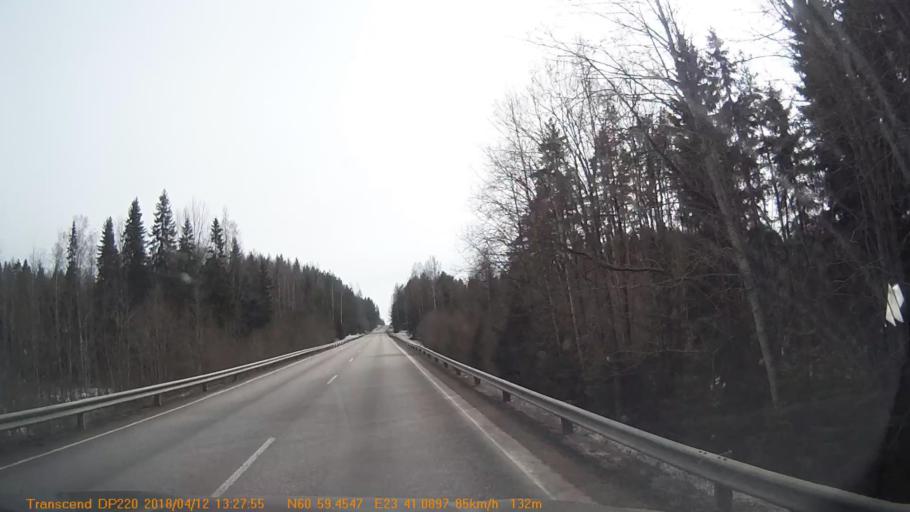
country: FI
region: Pirkanmaa
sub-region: Etelae-Pirkanmaa
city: Kylmaekoski
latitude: 60.9907
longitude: 23.6850
